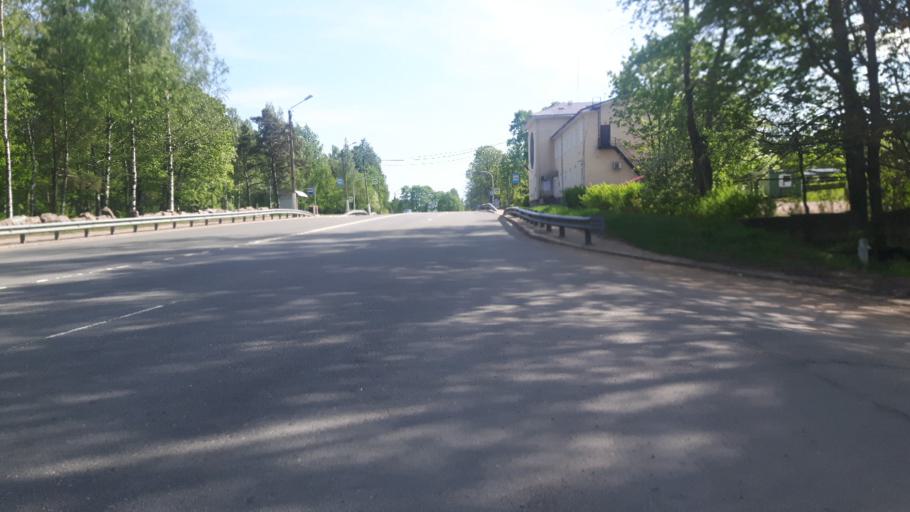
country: RU
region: Leningrad
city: Vyborg
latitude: 60.7323
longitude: 28.6980
